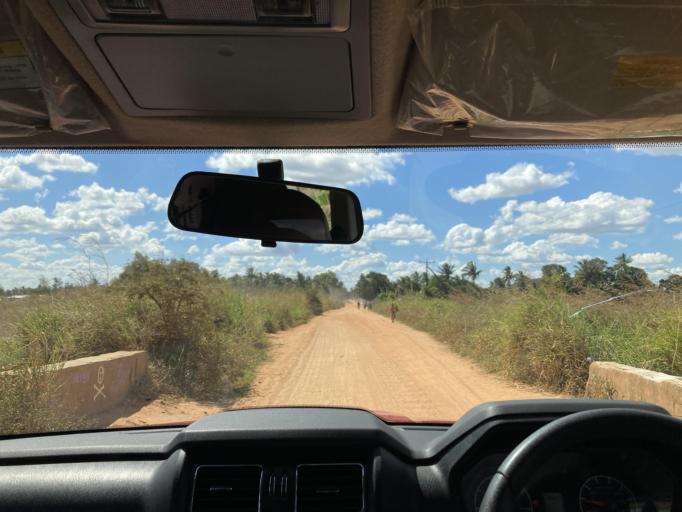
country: MZ
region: Cabo Delgado
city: Montepuez
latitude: -13.1474
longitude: 38.9919
